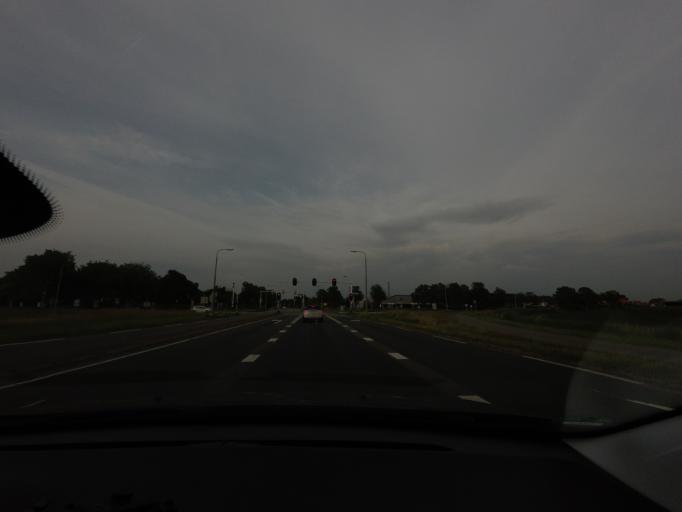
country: NL
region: Zeeland
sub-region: Schouwen-Duiveland
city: Bruinisse
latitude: 51.6456
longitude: 3.9990
